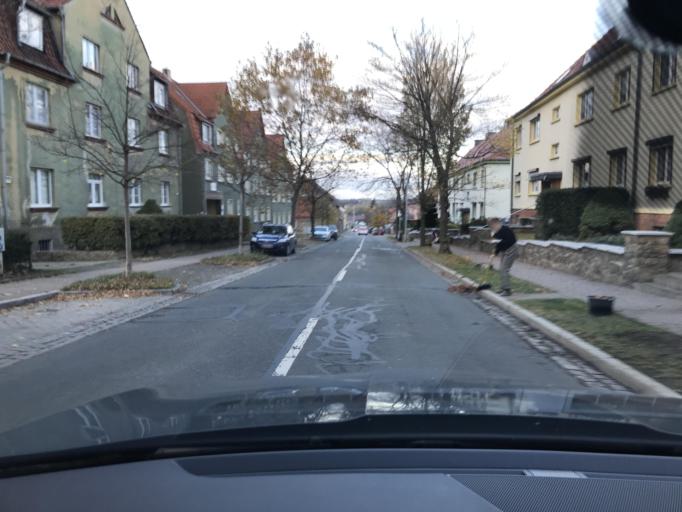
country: DE
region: Saxony-Anhalt
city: Thale
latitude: 51.7471
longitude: 11.0394
